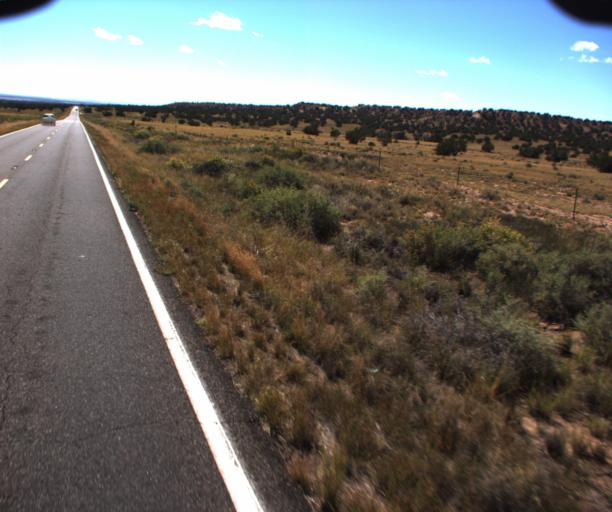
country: US
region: Arizona
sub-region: Apache County
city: Saint Johns
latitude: 34.8010
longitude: -109.2380
